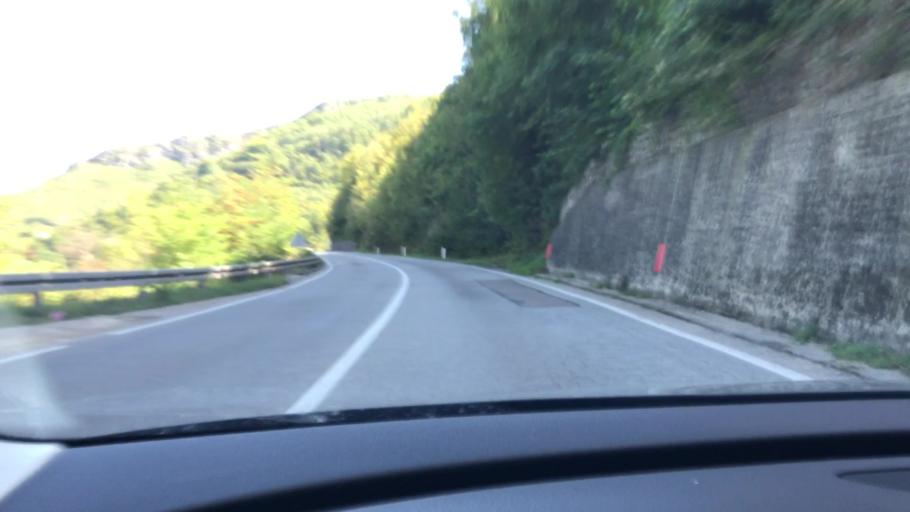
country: BA
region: Federation of Bosnia and Herzegovina
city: Jablanica
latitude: 43.6832
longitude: 17.7982
